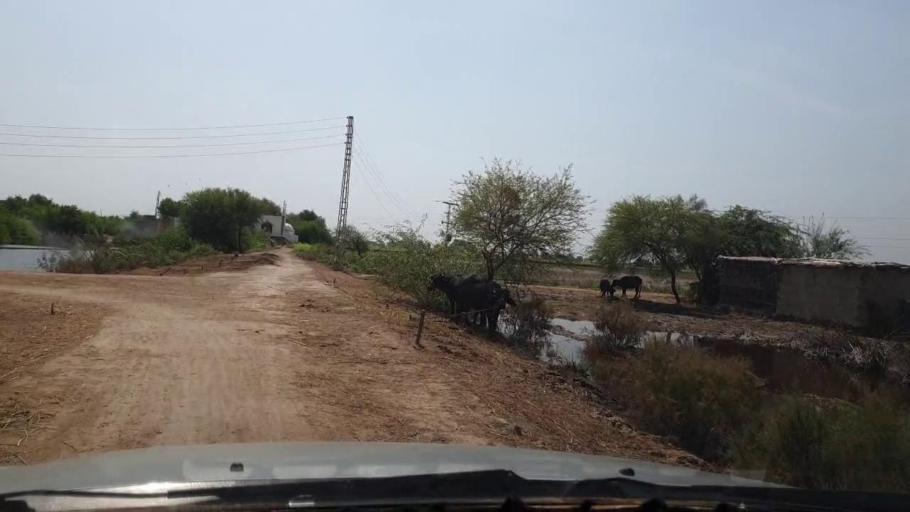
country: PK
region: Sindh
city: Tando Muhammad Khan
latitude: 25.1569
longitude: 68.6368
